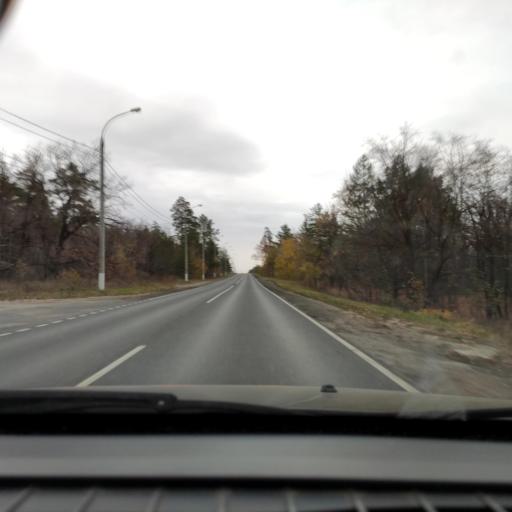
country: RU
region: Samara
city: Tol'yatti
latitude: 53.4740
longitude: 49.4088
